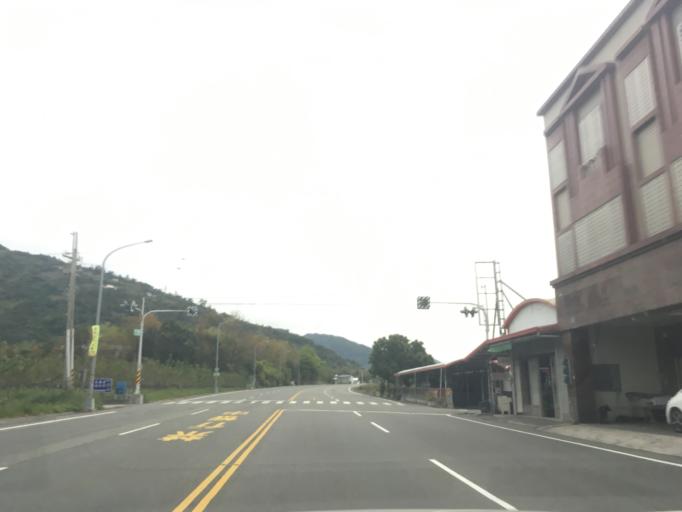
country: TW
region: Taiwan
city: Taitung City
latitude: 22.7298
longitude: 121.0561
